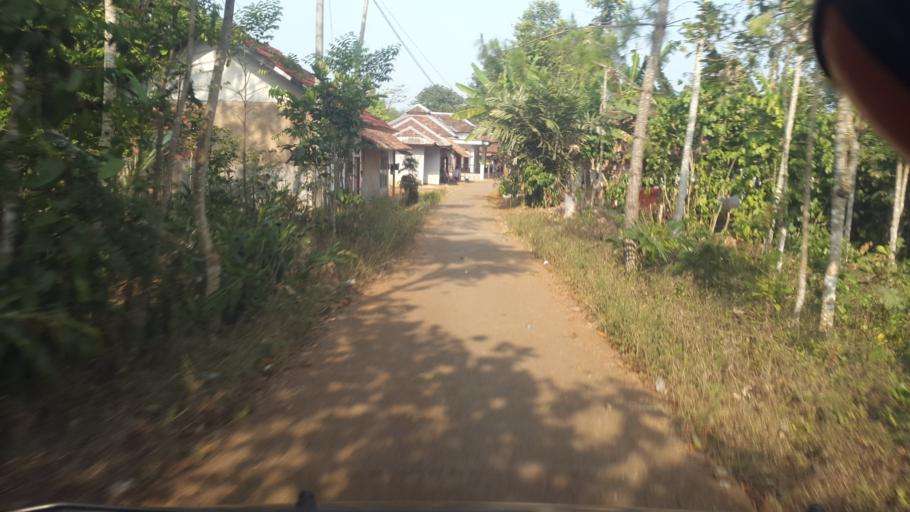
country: ID
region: West Java
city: Cipari Satu
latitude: -7.1133
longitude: 106.8607
